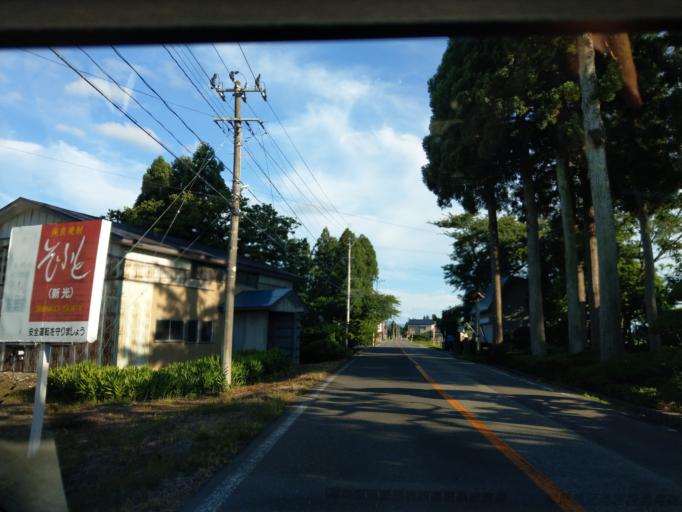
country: JP
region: Akita
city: Kakunodatemachi
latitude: 39.5658
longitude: 140.5833
